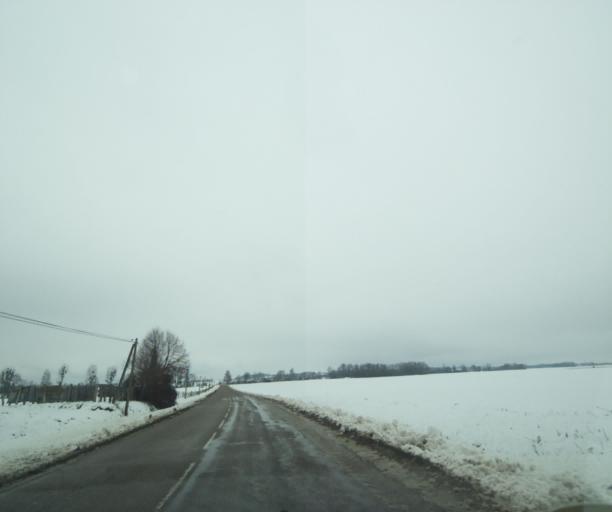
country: FR
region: Champagne-Ardenne
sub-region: Departement de la Haute-Marne
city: Montier-en-Der
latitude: 48.4481
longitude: 4.7971
